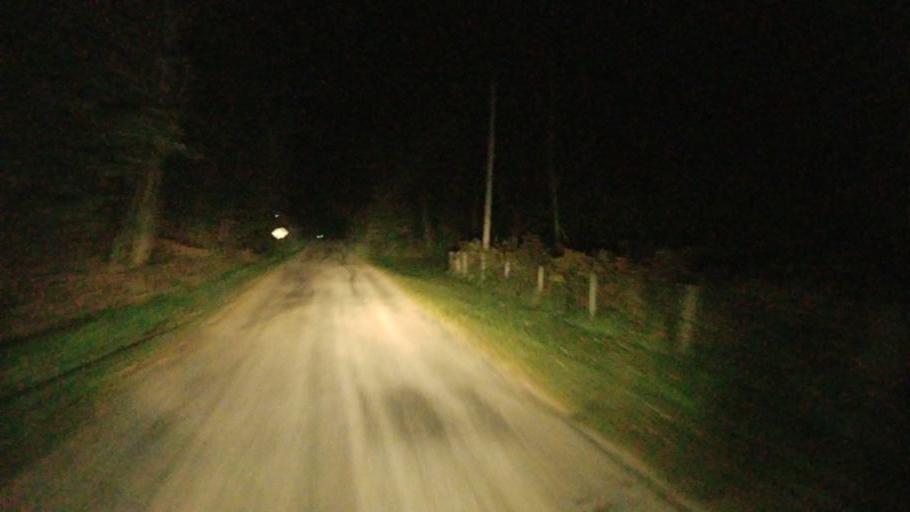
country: US
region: Ohio
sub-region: Ashland County
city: Loudonville
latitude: 40.5831
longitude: -82.3568
